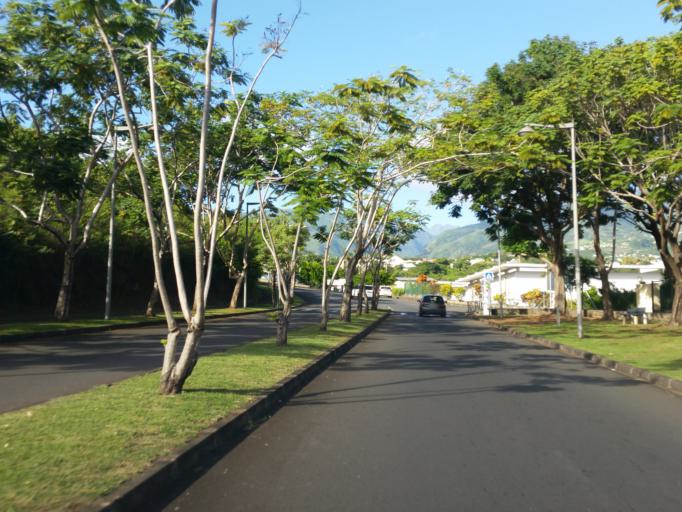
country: RE
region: Reunion
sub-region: Reunion
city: Sainte-Marie
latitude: -20.9033
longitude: 55.4999
